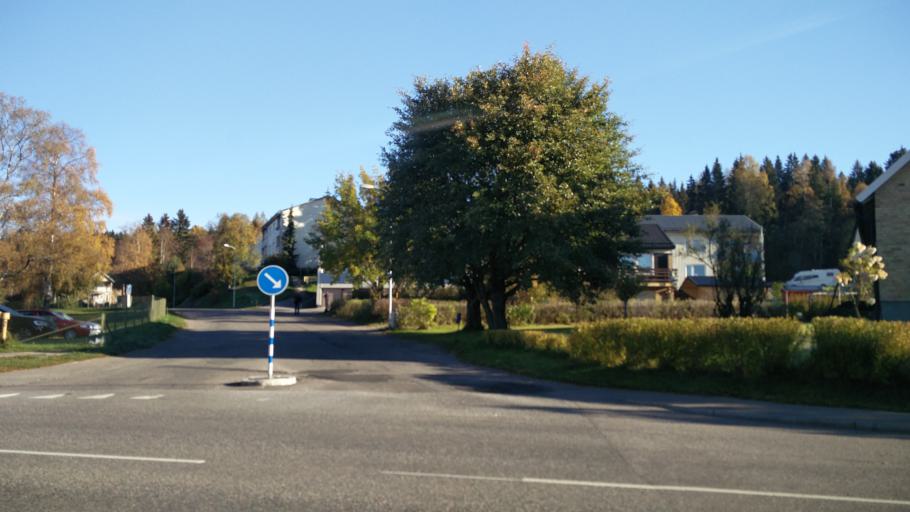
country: SE
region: Vaesternorrland
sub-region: Sundsvalls Kommun
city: Sundsvall
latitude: 62.4020
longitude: 17.2652
